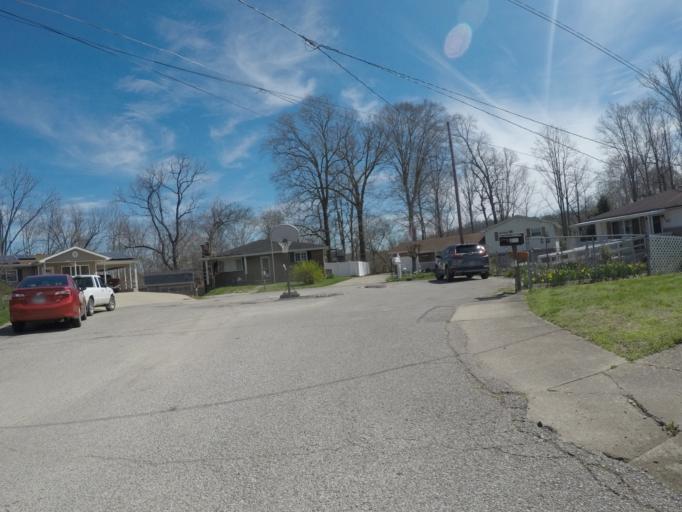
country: US
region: West Virginia
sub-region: Cabell County
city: Pea Ridge
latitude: 38.4105
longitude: -82.3191
